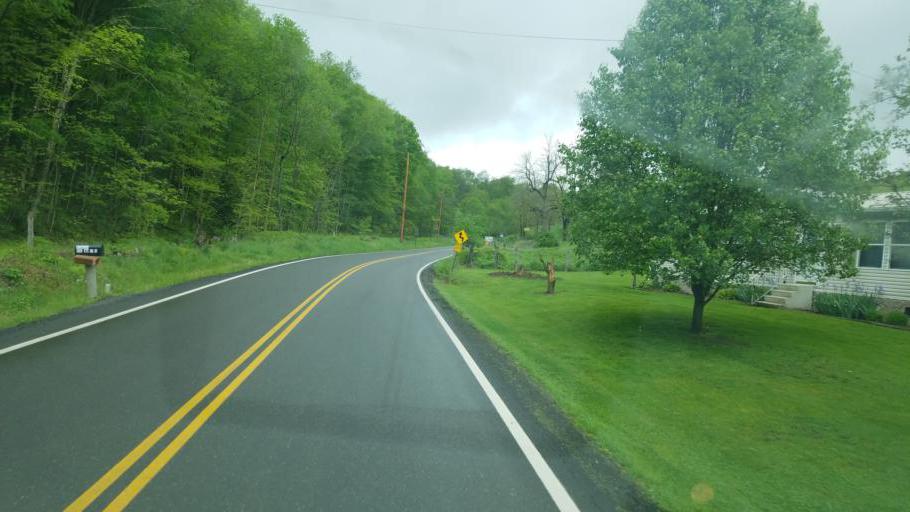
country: US
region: Ohio
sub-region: Harrison County
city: Cadiz
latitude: 40.2721
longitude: -80.8517
